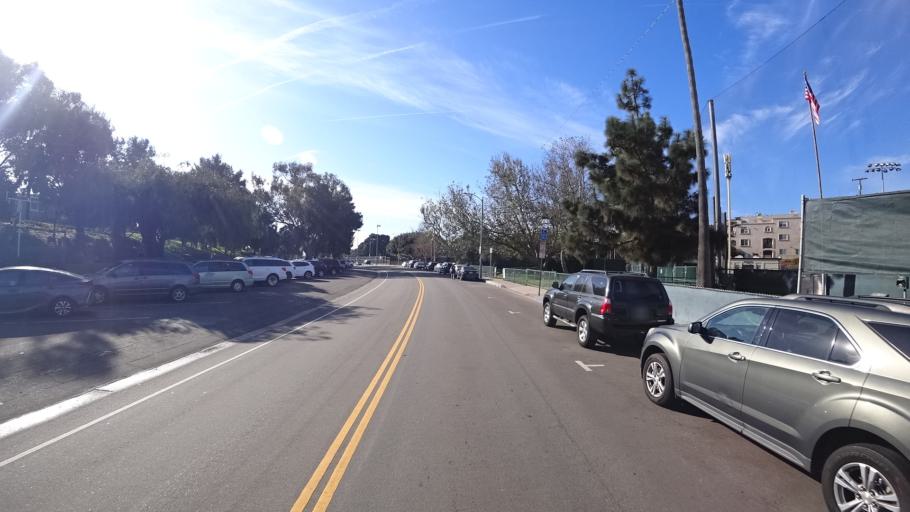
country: US
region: California
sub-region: Los Angeles County
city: Manhattan Beach
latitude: 33.8911
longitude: -118.4100
